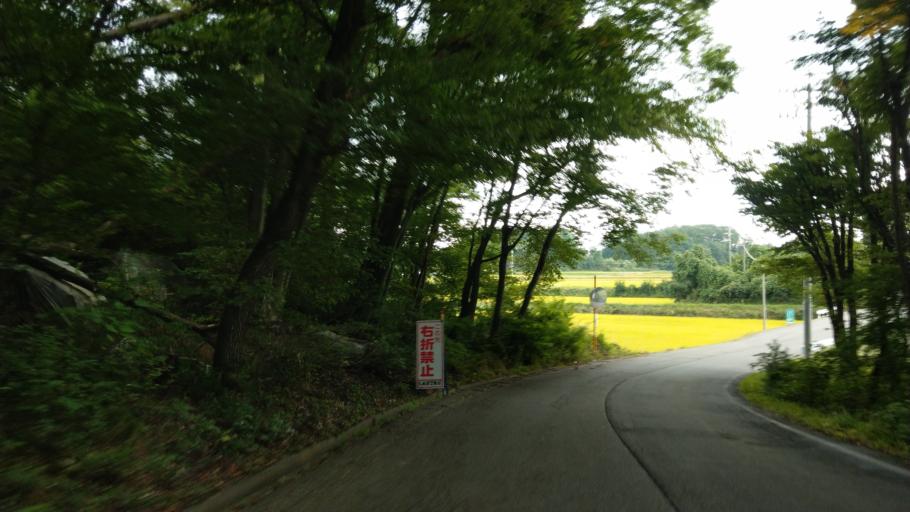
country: JP
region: Nagano
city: Komoro
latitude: 36.3104
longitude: 138.3931
